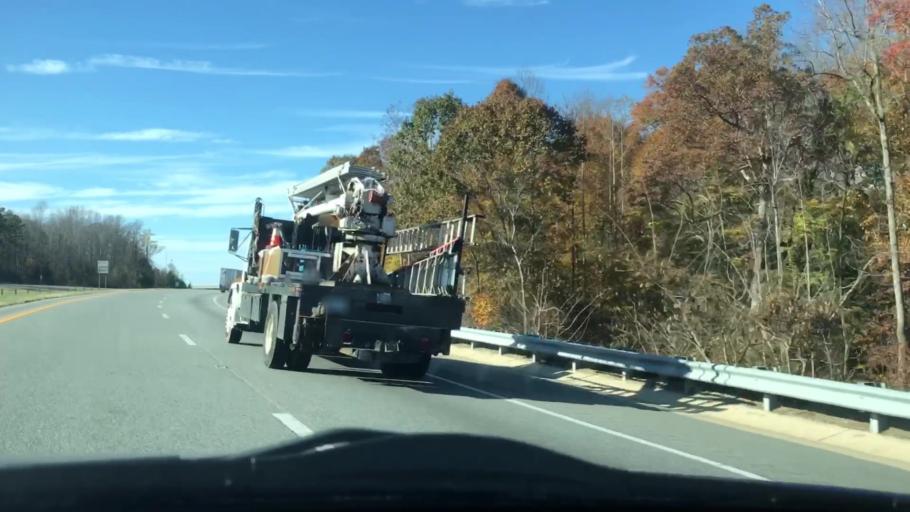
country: US
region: North Carolina
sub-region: Randolph County
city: Archdale
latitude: 35.9357
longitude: -79.9577
